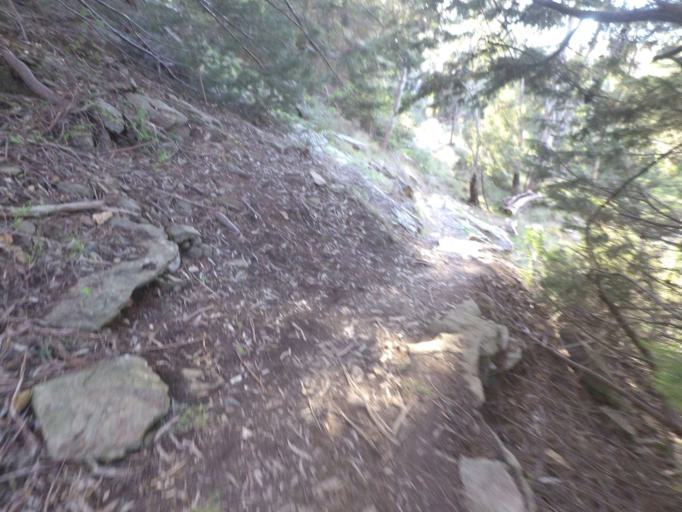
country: AU
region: Victoria
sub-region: Mount Alexander
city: Castlemaine
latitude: -37.1623
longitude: 144.2144
